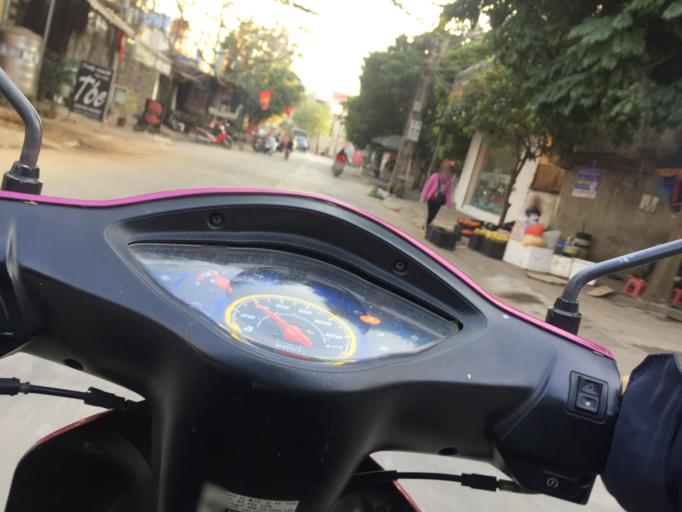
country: VN
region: Ha Noi
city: Chuc Son
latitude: 20.9158
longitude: 105.7141
